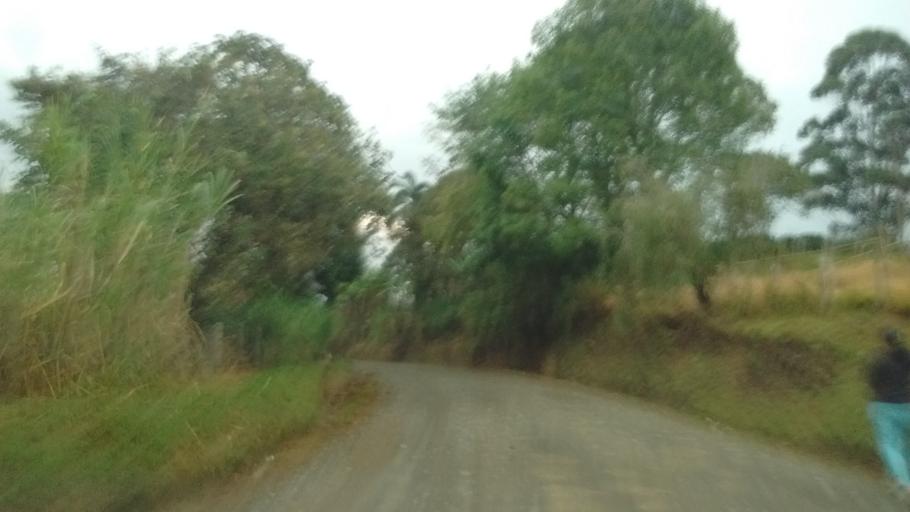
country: CO
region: Cauca
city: Lopez
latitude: 2.3950
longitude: -76.7435
